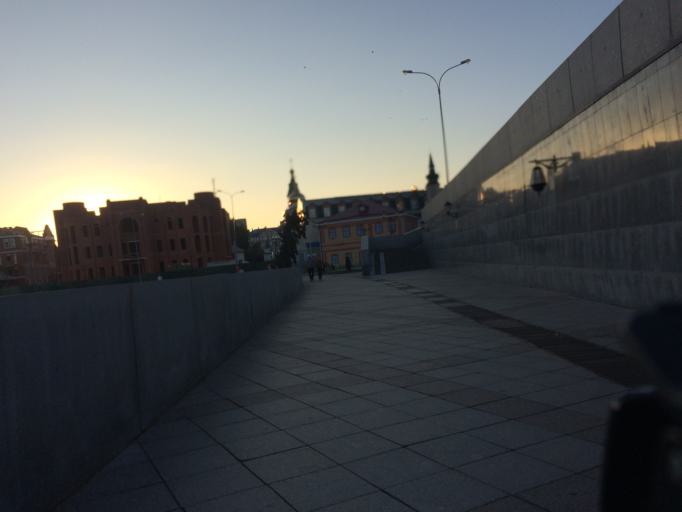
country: RU
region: Mariy-El
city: Yoshkar-Ola
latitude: 56.6325
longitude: 47.9019
